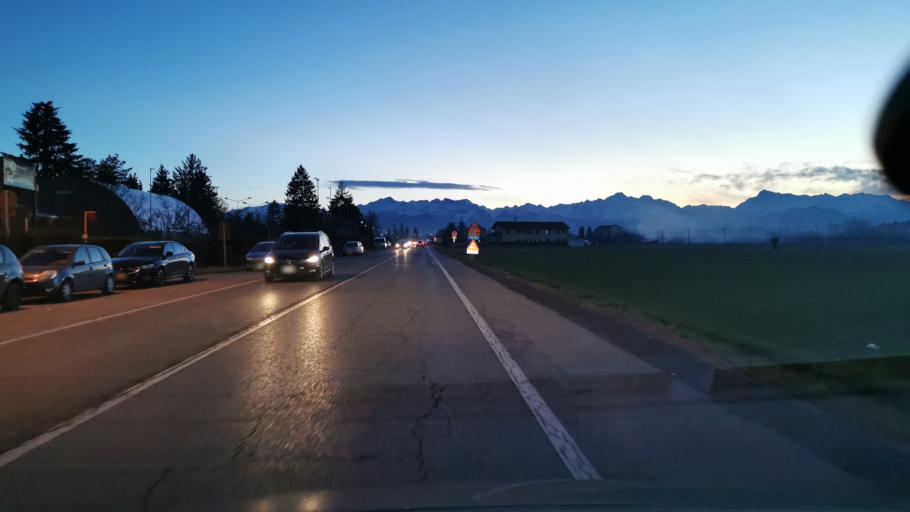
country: IT
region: Piedmont
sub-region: Provincia di Cuneo
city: Roata Rossi
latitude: 44.4397
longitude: 7.5636
